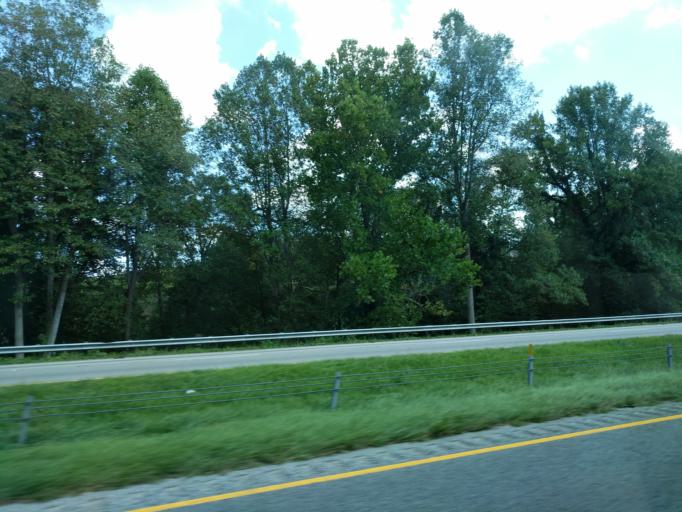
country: US
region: South Carolina
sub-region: Spartanburg County
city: Roebuck
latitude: 34.8485
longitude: -81.9752
